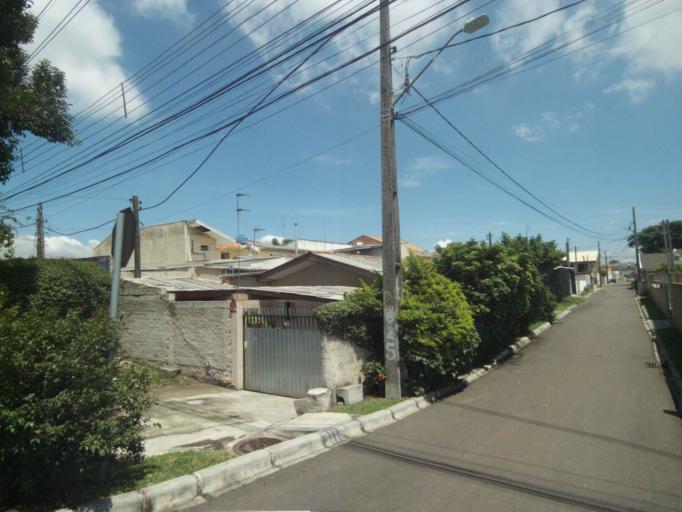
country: BR
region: Parana
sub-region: Pinhais
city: Pinhais
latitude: -25.4764
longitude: -49.1922
